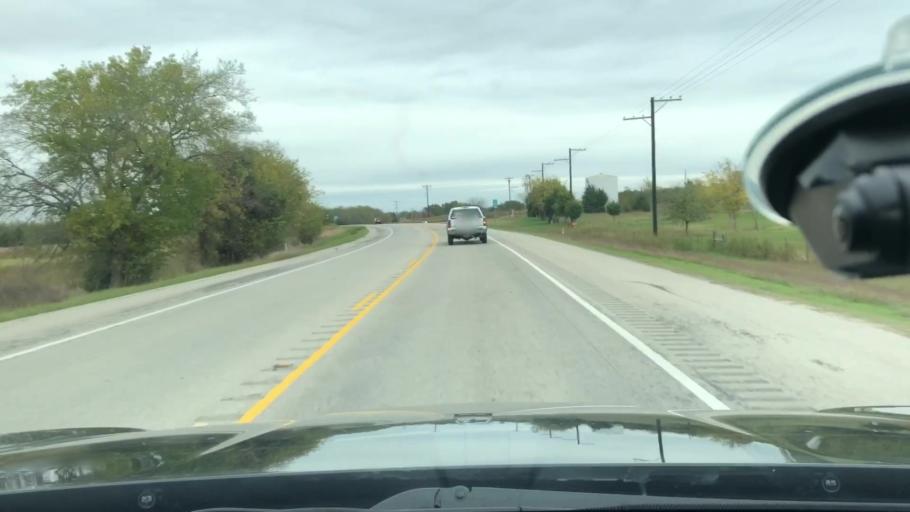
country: US
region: Texas
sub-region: Hunt County
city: Greenville
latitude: 33.0599
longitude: -96.1096
